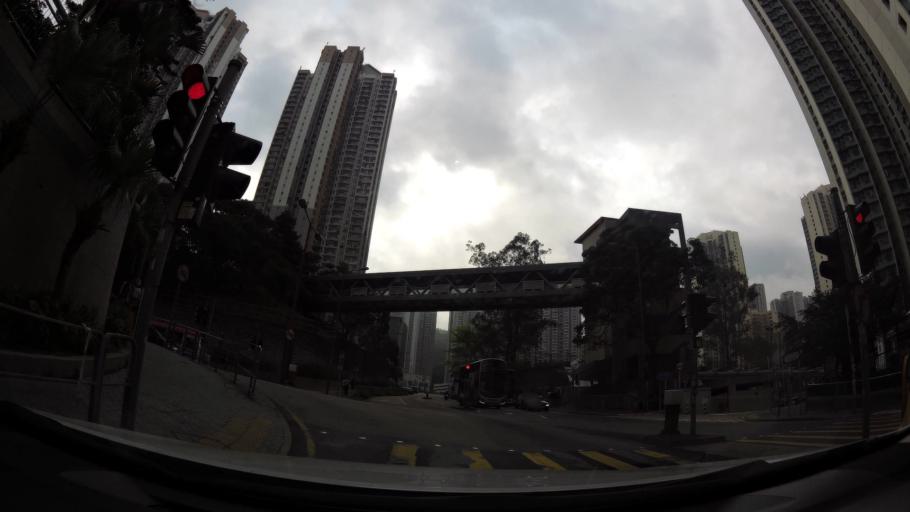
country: HK
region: Kowloon City
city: Kowloon
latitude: 22.3100
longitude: 114.2350
